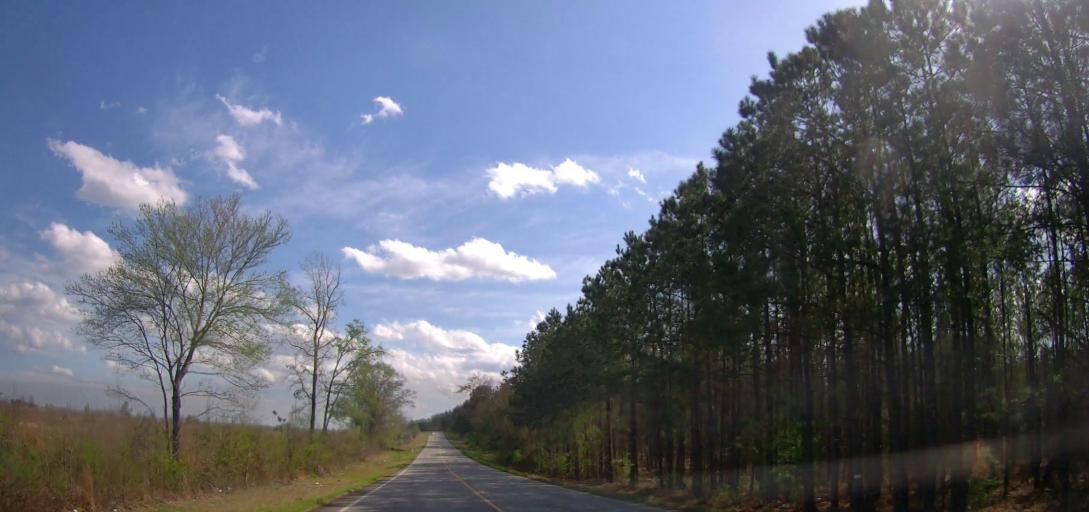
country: US
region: Georgia
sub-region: Wilkinson County
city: Gordon
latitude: 32.9523
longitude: -83.2904
